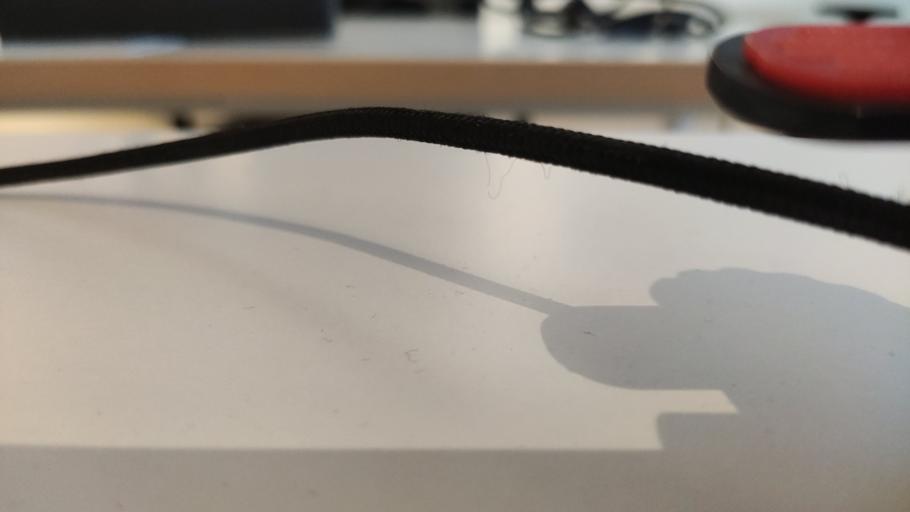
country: RU
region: Moskovskaya
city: Sychevo
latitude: 55.8390
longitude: 36.3332
